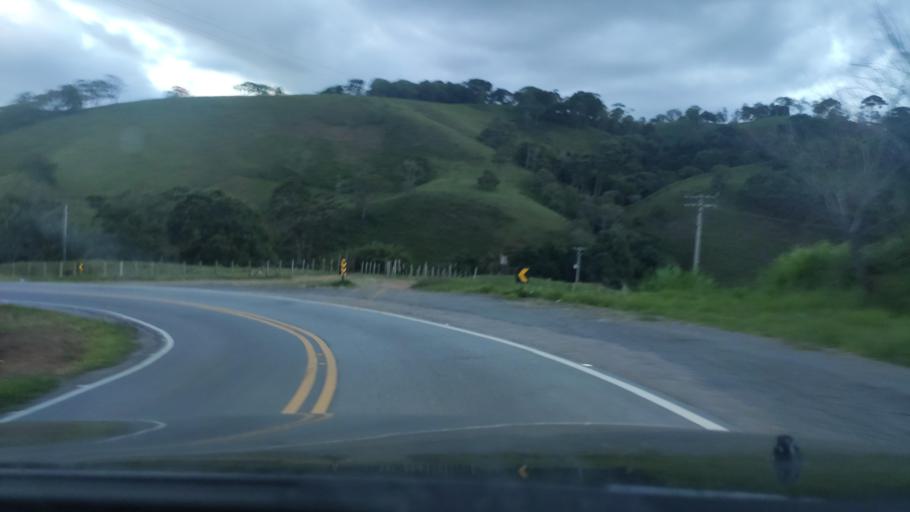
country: BR
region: Sao Paulo
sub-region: Campos Do Jordao
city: Campos do Jordao
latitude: -22.8261
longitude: -45.7157
